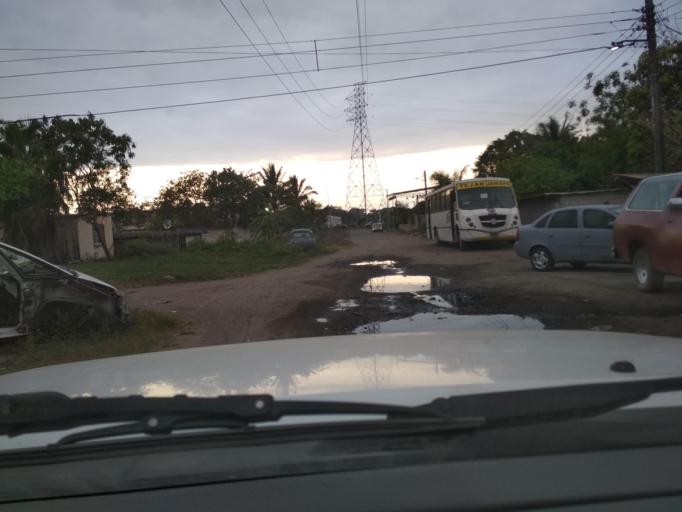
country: MX
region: Veracruz
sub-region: Medellin
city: Fraccionamiento Arboledas San Ramon
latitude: 19.0845
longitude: -96.1547
